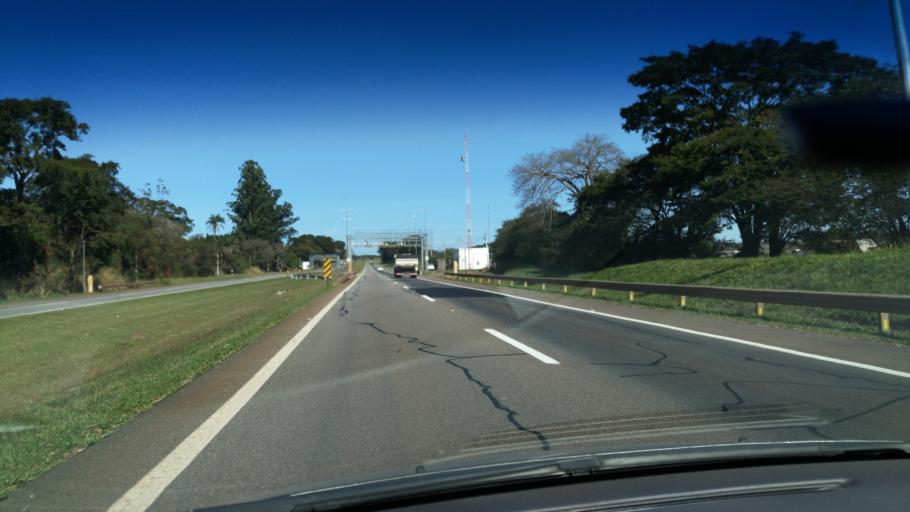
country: BR
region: Sao Paulo
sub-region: Santo Antonio De Posse
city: Santo Antonio de Posse
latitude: -22.5616
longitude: -47.0002
